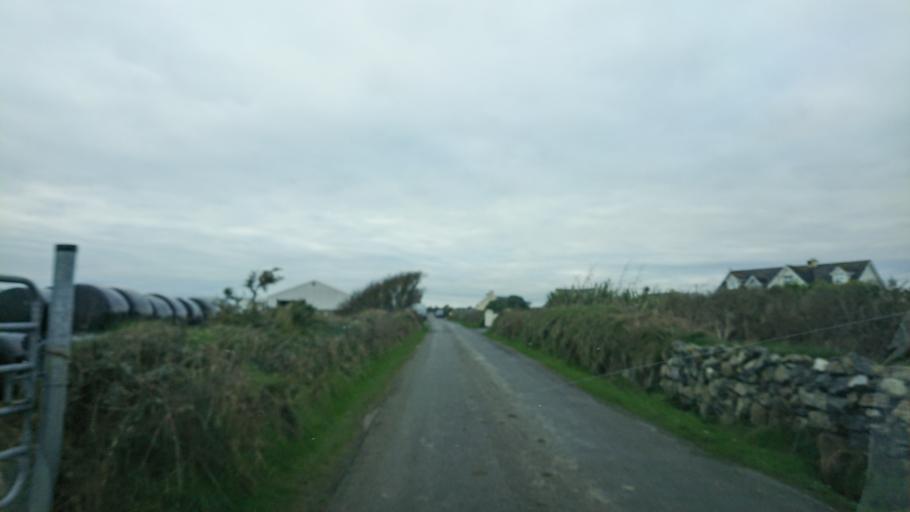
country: IE
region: Munster
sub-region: Waterford
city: Tra Mhor
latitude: 52.1379
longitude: -7.1806
